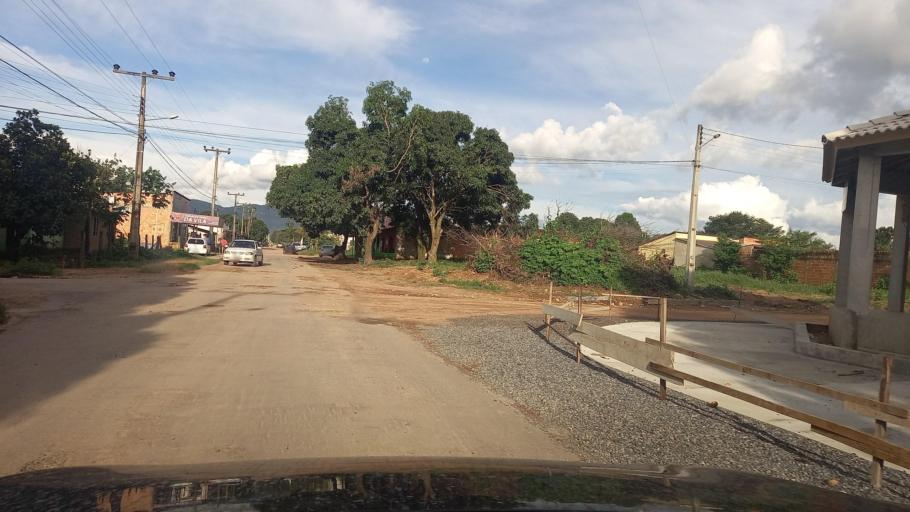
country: BR
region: Goias
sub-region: Cavalcante
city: Cavalcante
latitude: -13.7977
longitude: -47.4456
